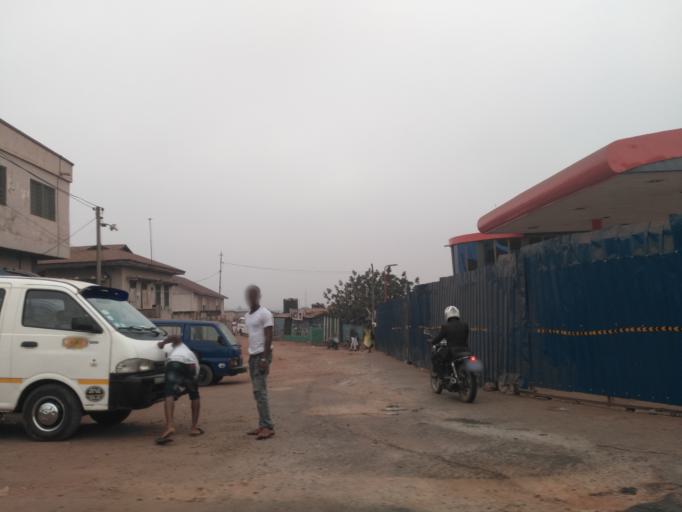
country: GH
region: Ashanti
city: Tafo
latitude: 6.7141
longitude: -1.6078
